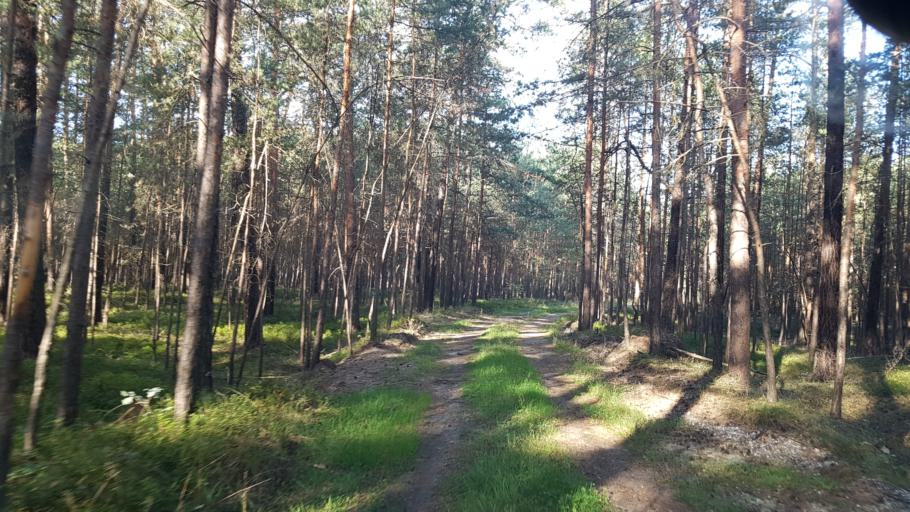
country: DE
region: Brandenburg
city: Finsterwalde
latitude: 51.5843
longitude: 13.6721
